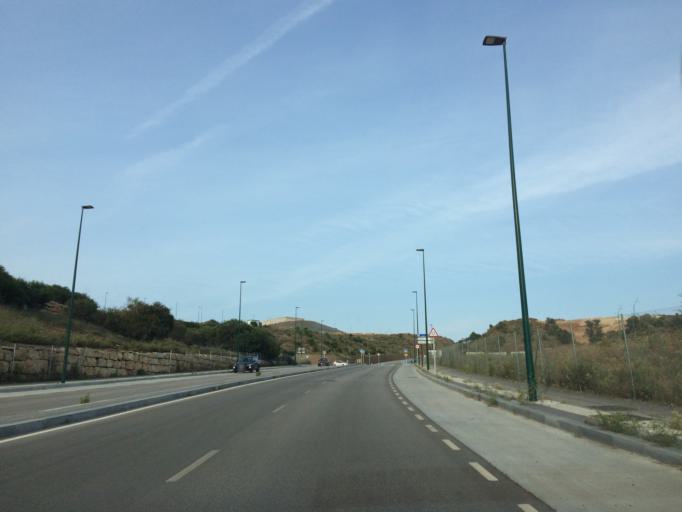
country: ES
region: Andalusia
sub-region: Provincia de Malaga
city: Malaga
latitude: 36.7368
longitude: -4.4026
